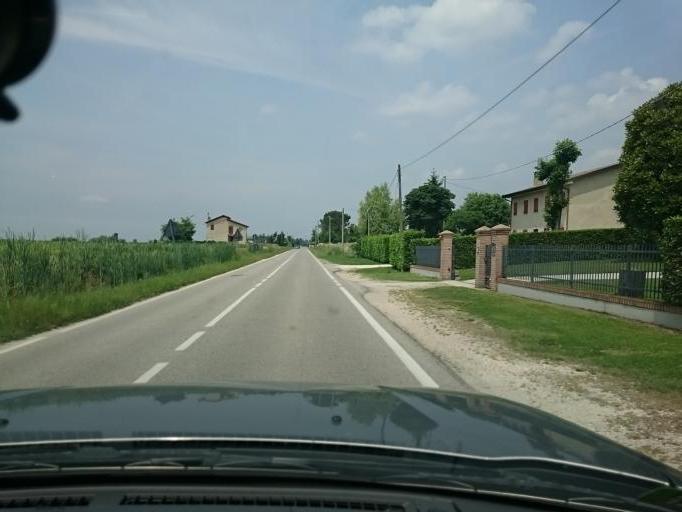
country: IT
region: Veneto
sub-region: Provincia di Padova
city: Brugine
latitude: 45.3118
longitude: 11.9940
